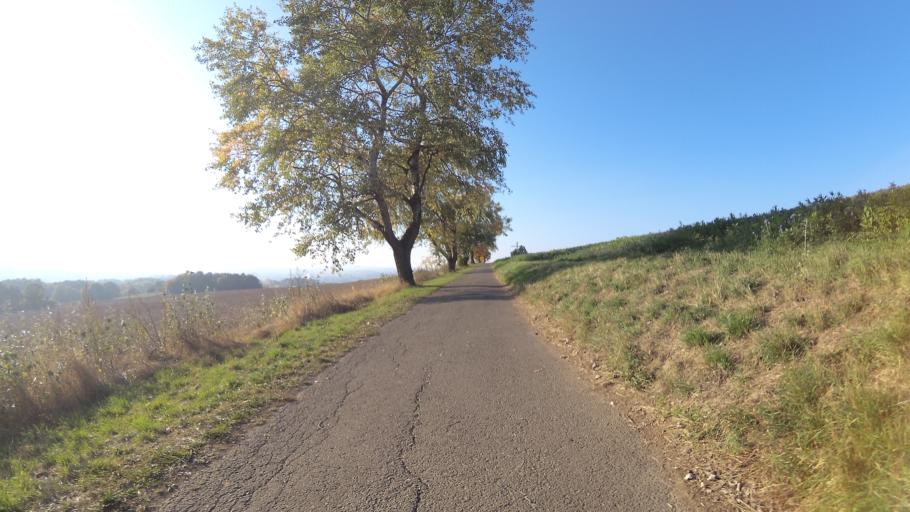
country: DE
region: Saarland
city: Sankt Wendel
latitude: 49.4564
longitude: 7.1908
